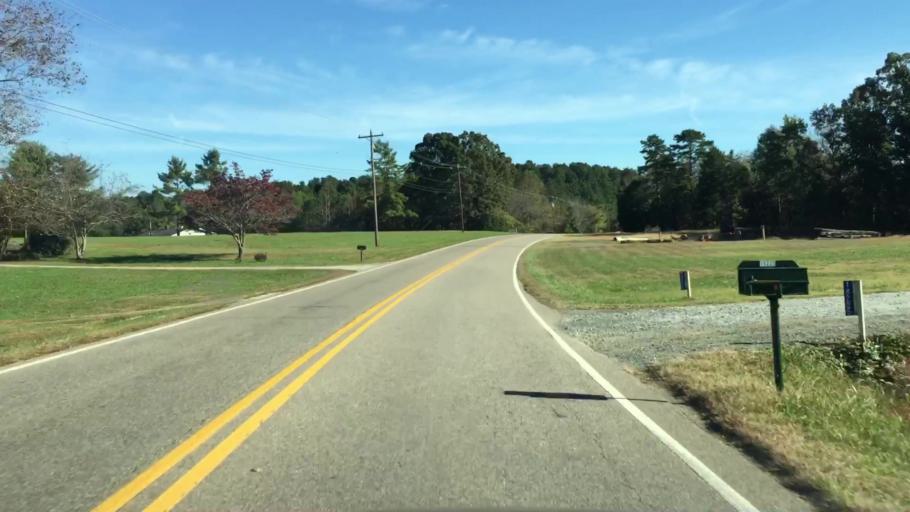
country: US
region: North Carolina
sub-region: Iredell County
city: Mooresville
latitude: 35.6126
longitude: -80.7542
